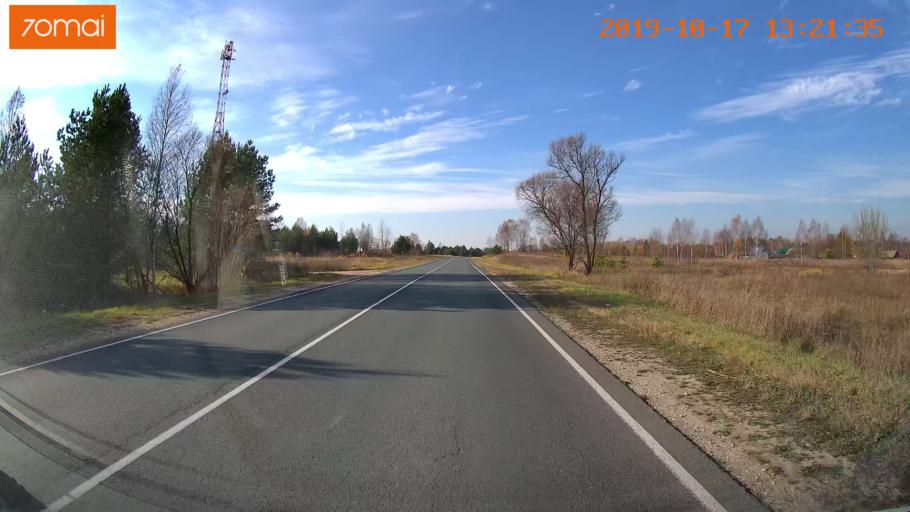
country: RU
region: Rjazan
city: Gus'-Zheleznyy
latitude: 55.0815
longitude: 41.0235
